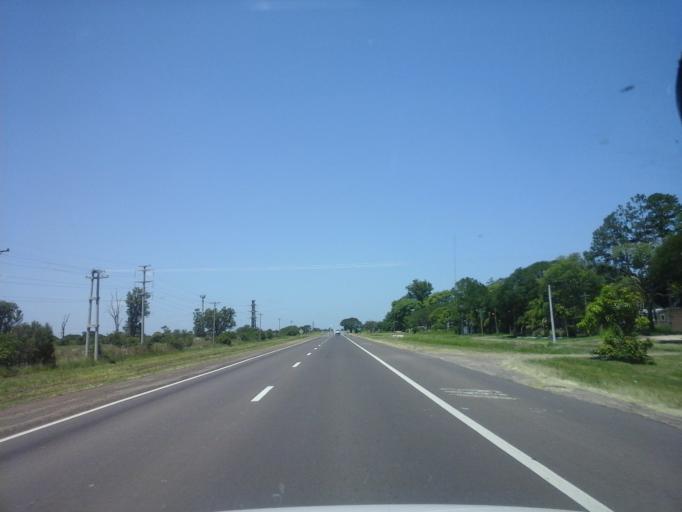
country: AR
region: Corrientes
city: Corrientes
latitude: -27.4274
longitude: -58.7189
